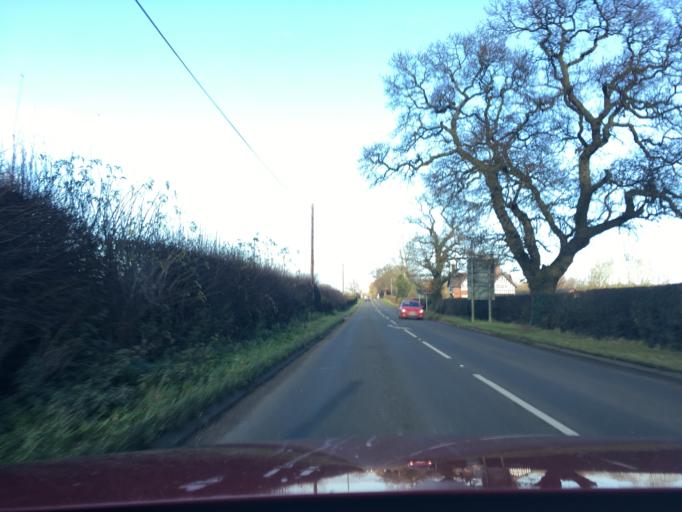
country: GB
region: England
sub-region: Staffordshire
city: Barton under Needwood
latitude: 52.8054
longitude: -1.7375
